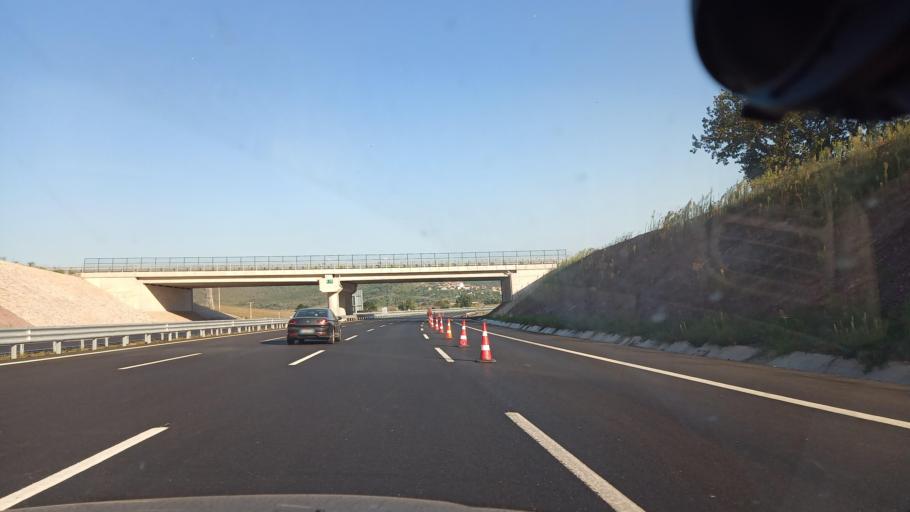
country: TR
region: Sakarya
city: Adapazari
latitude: 40.8383
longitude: 30.3807
